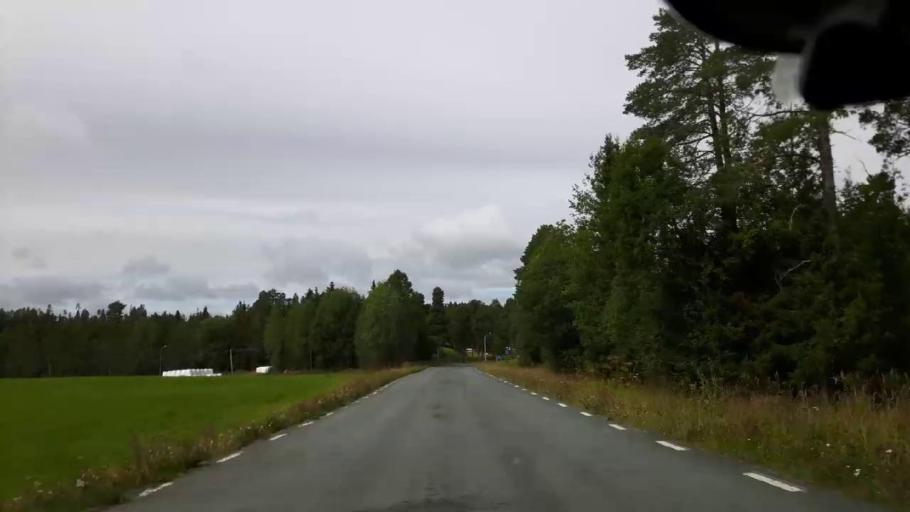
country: SE
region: Jaemtland
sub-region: Krokoms Kommun
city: Valla
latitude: 63.4602
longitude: 14.0354
